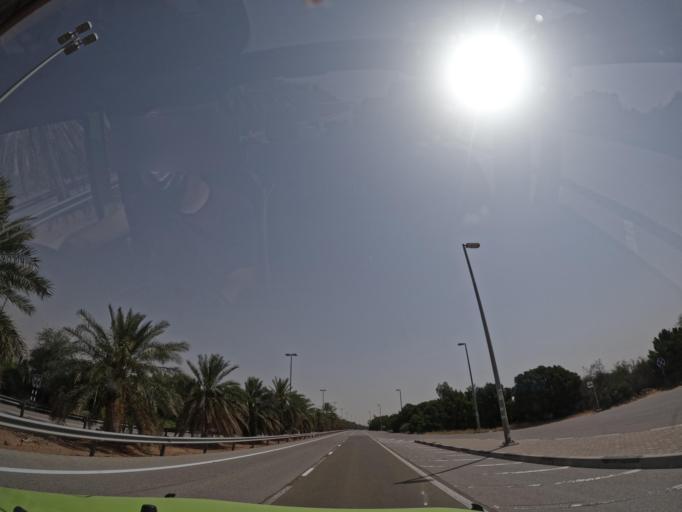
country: OM
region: Al Buraimi
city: Al Buraymi
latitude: 24.6912
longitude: 55.7288
